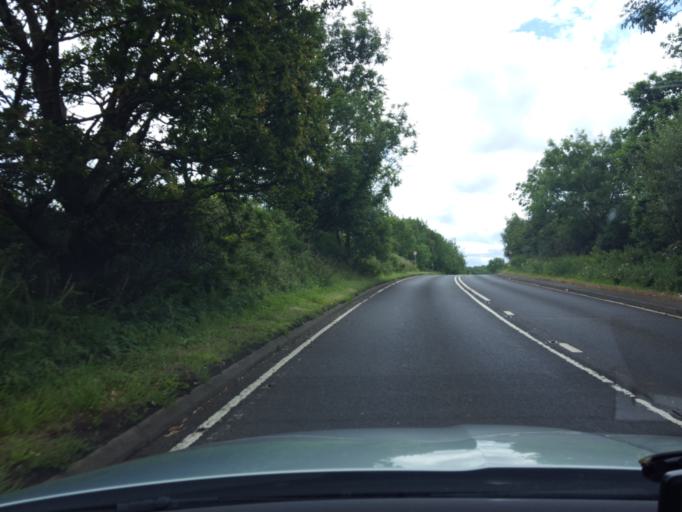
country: GB
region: Scotland
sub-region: Stirling
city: Cowie
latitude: 56.0536
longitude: -3.8615
